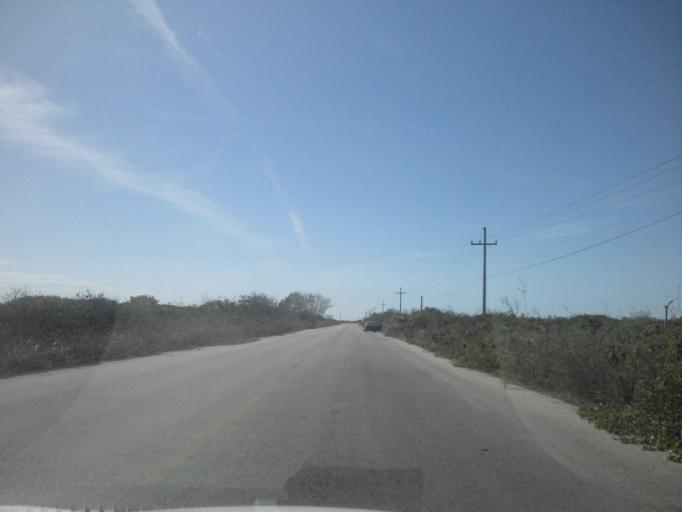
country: MX
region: Yucatan
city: Telchac Puerto
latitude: 21.3321
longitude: -89.3565
